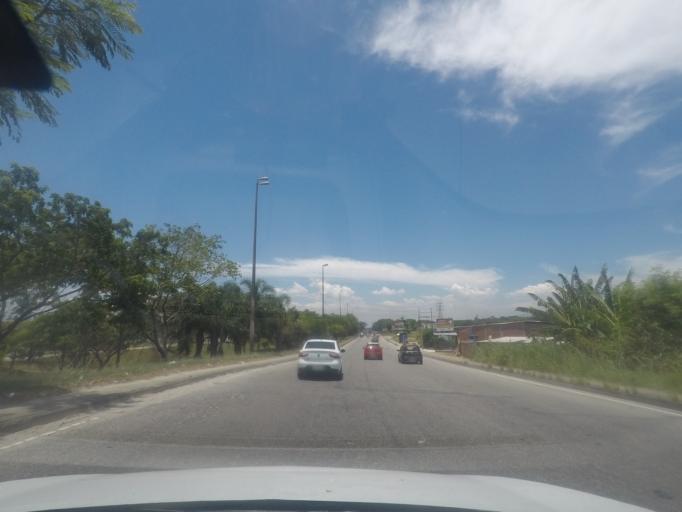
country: BR
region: Rio de Janeiro
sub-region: Itaguai
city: Itaguai
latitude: -22.8952
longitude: -43.6796
